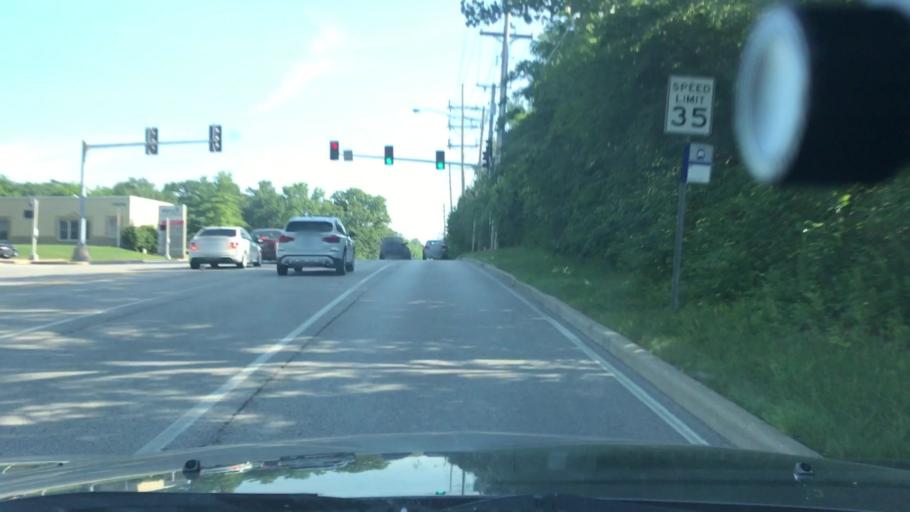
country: US
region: Missouri
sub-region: Saint Louis County
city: Creve Coeur
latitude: 38.6465
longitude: -90.4433
